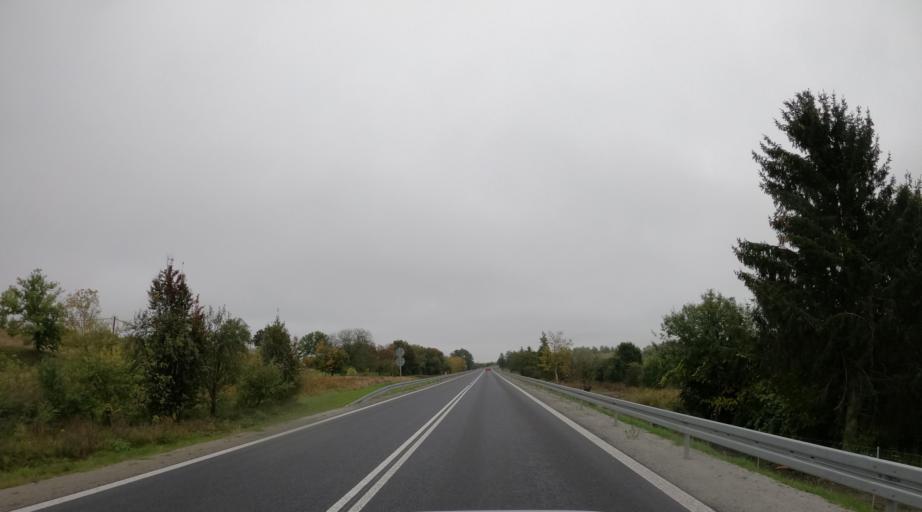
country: PL
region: West Pomeranian Voivodeship
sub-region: Powiat mysliborski
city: Mysliborz
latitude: 52.9290
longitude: 14.8881
